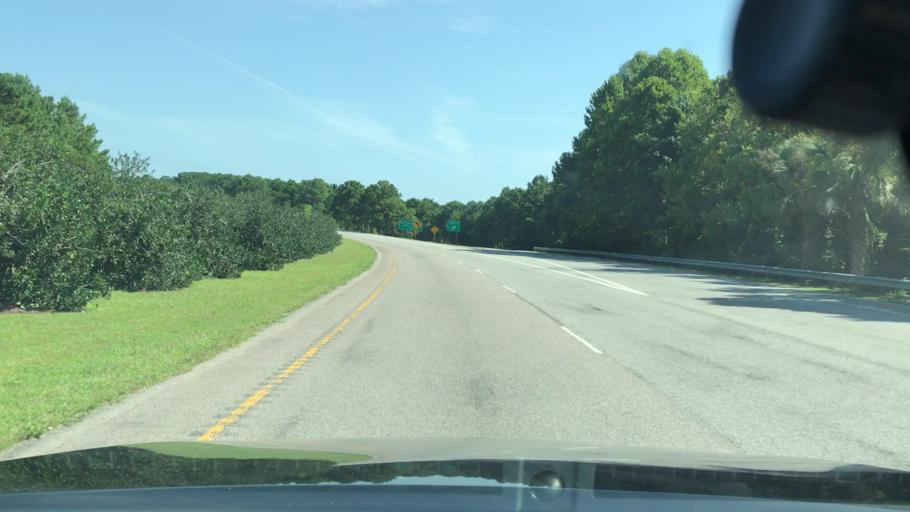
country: US
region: South Carolina
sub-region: Beaufort County
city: Hilton Head Island
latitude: 32.2108
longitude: -80.7385
